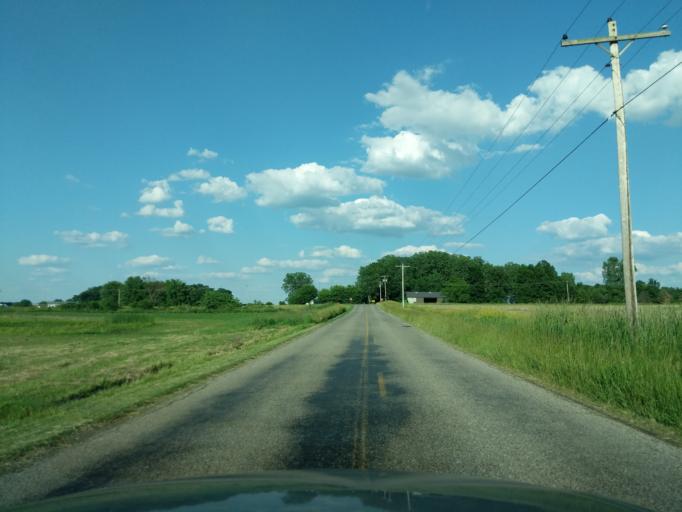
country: US
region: Indiana
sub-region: Whitley County
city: Tri-Lakes
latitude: 41.3026
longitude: -85.5028
